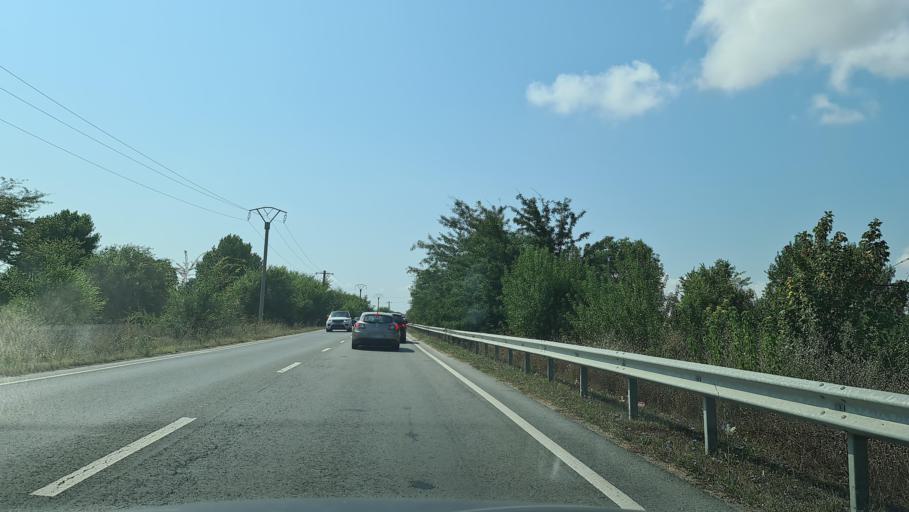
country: RO
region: Constanta
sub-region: Comuna Agigea
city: Agigea
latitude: 44.0900
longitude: 28.6400
